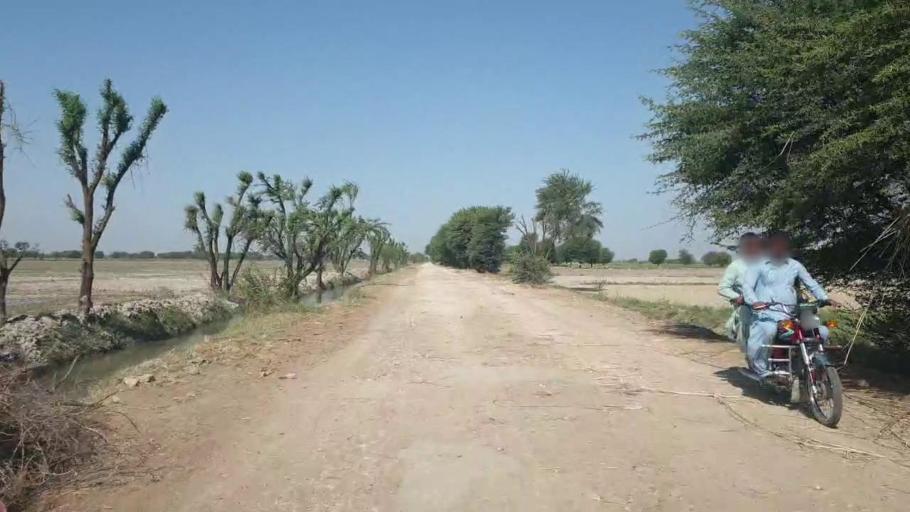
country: PK
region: Sindh
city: Umarkot
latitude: 25.2899
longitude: 69.6386
